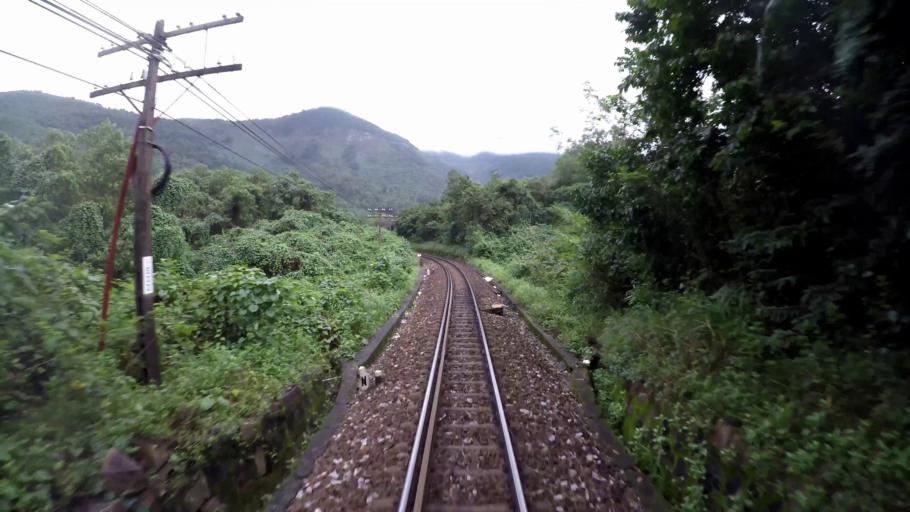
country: VN
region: Da Nang
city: Lien Chieu
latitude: 16.2073
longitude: 108.1201
